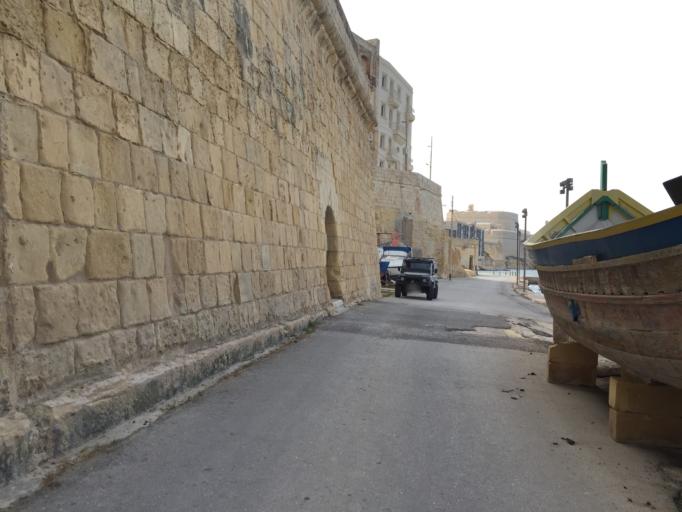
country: MT
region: Il-Birgu
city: Vittoriosa
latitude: 35.8892
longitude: 14.5227
